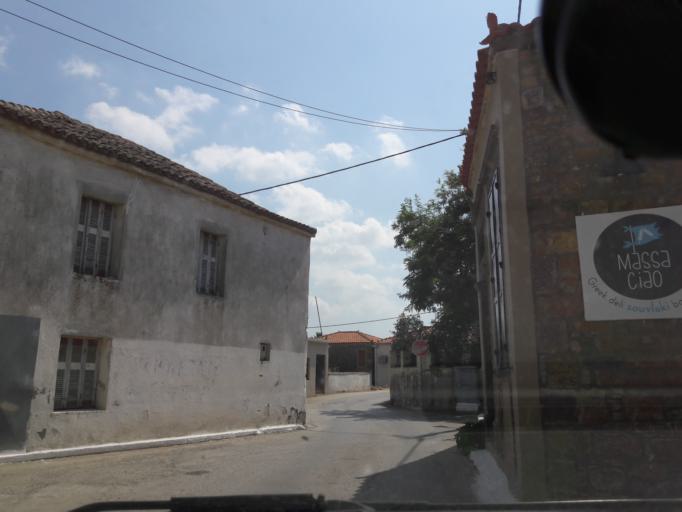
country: GR
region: North Aegean
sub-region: Nomos Lesvou
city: Myrina
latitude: 39.9272
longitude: 25.3333
